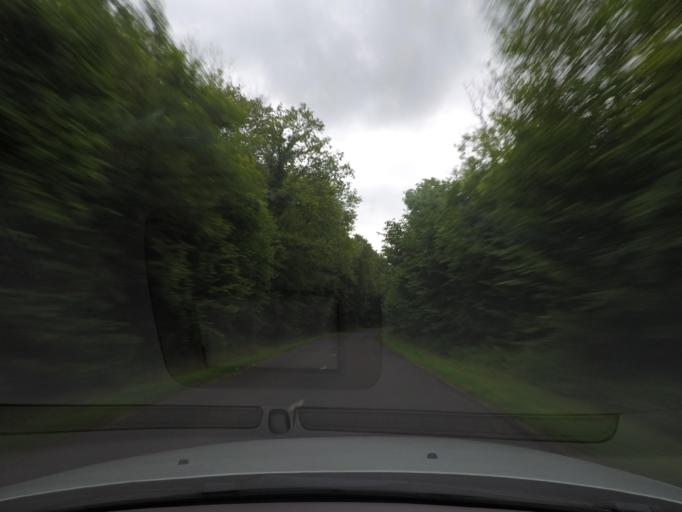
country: FR
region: Haute-Normandie
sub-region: Departement de la Seine-Maritime
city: Neufchatel-en-Bray
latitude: 49.7363
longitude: 1.4725
